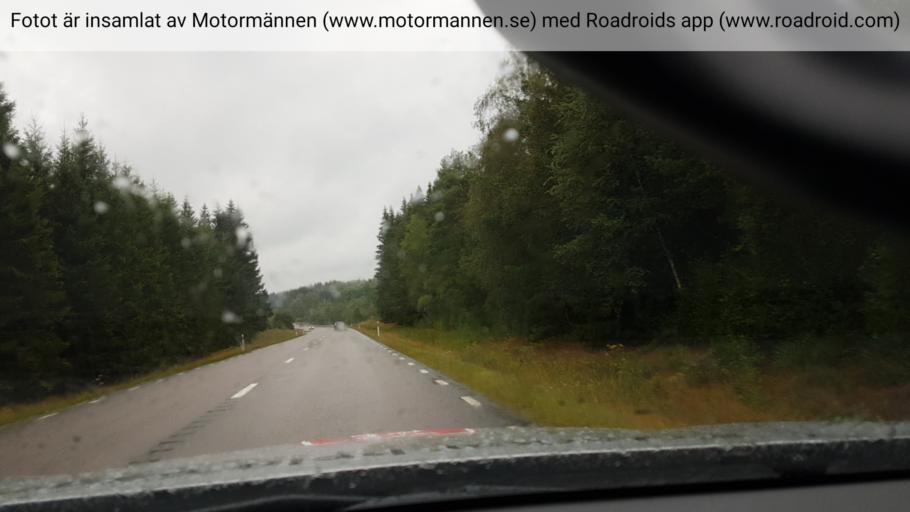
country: SE
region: Vaestra Goetaland
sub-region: Dals-Ed Kommun
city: Ed
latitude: 58.8923
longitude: 11.9242
